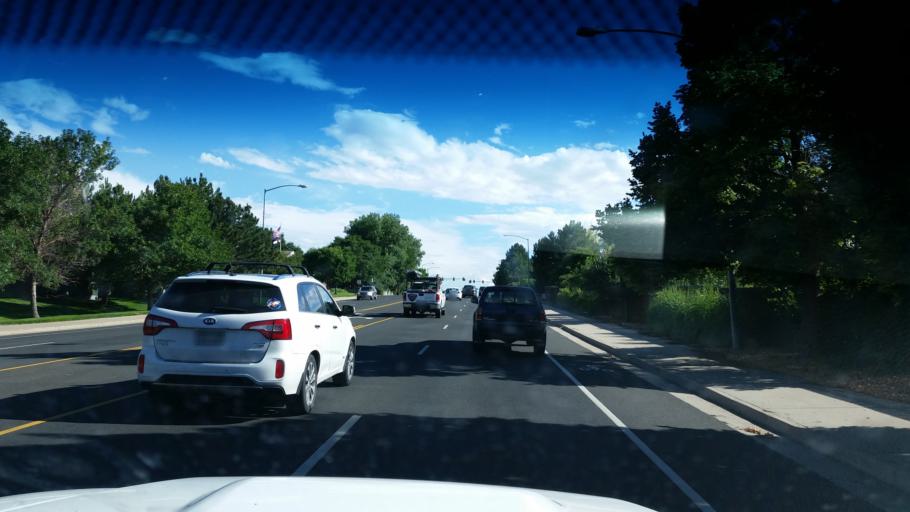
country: US
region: Colorado
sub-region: Adams County
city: Northglenn
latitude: 39.9196
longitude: -104.9404
